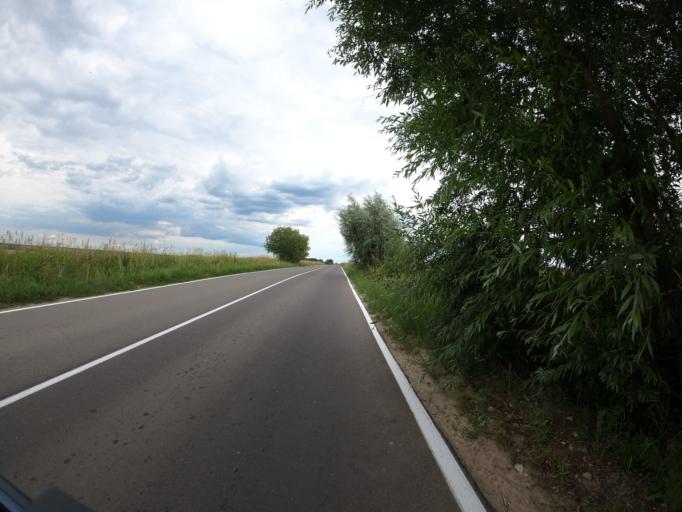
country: RU
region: Moskovskaya
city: Bronnitsy
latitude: 55.4877
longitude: 38.2461
